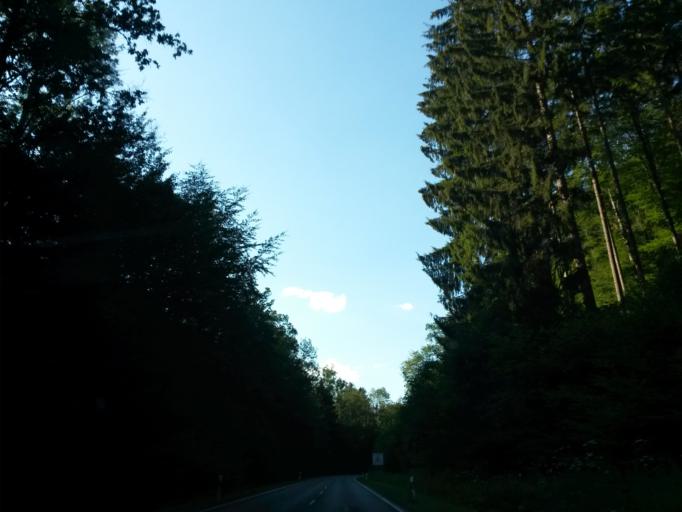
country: DE
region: North Rhine-Westphalia
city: Meinerzhagen
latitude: 51.0759
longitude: 7.6478
